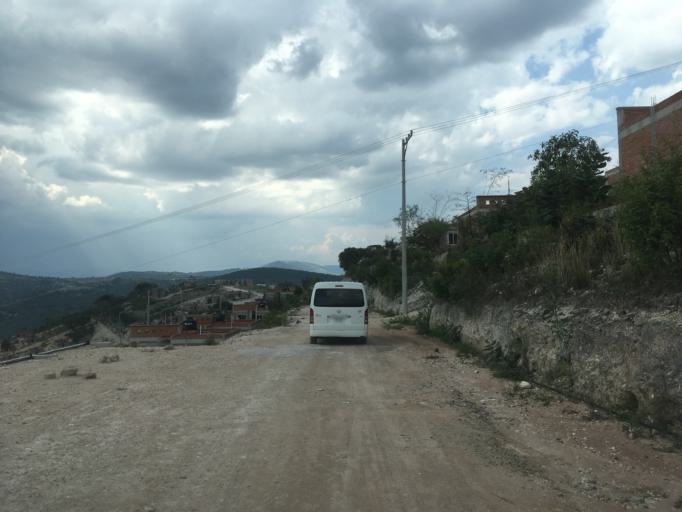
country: MX
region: Oaxaca
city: Santiago Tilantongo
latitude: 17.2203
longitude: -97.2715
